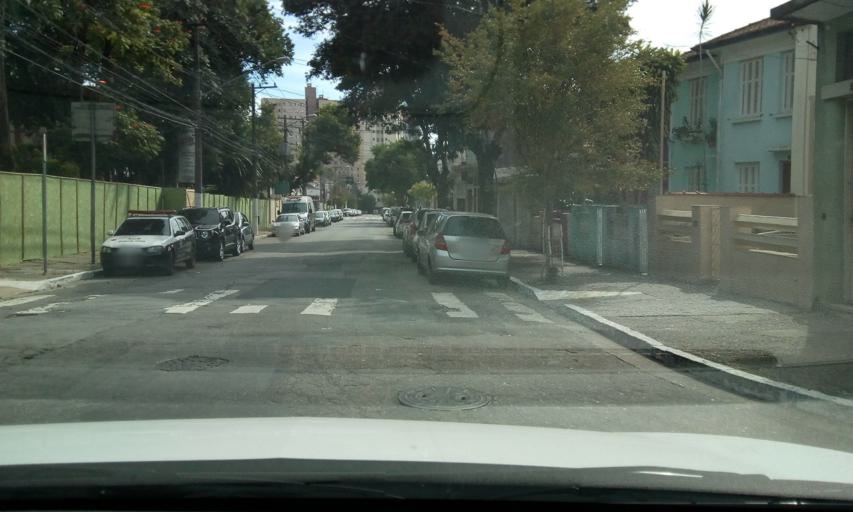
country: BR
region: Sao Paulo
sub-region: Sao Paulo
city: Sao Paulo
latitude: -23.5487
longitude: -46.5933
